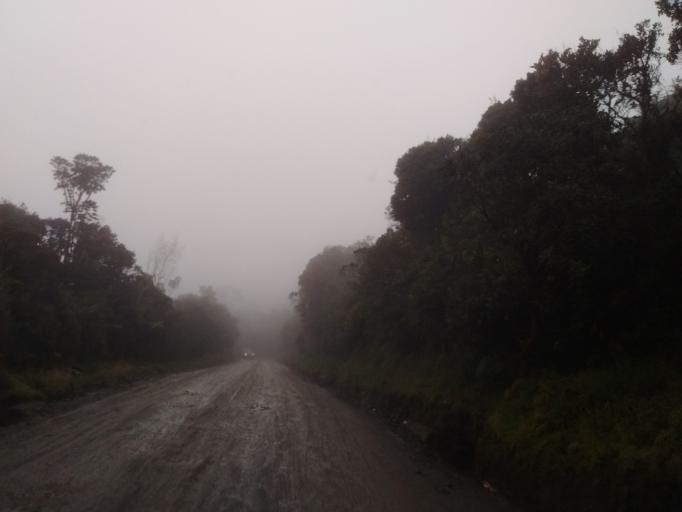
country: CO
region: Cauca
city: Paispamba
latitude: 2.1482
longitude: -76.4357
